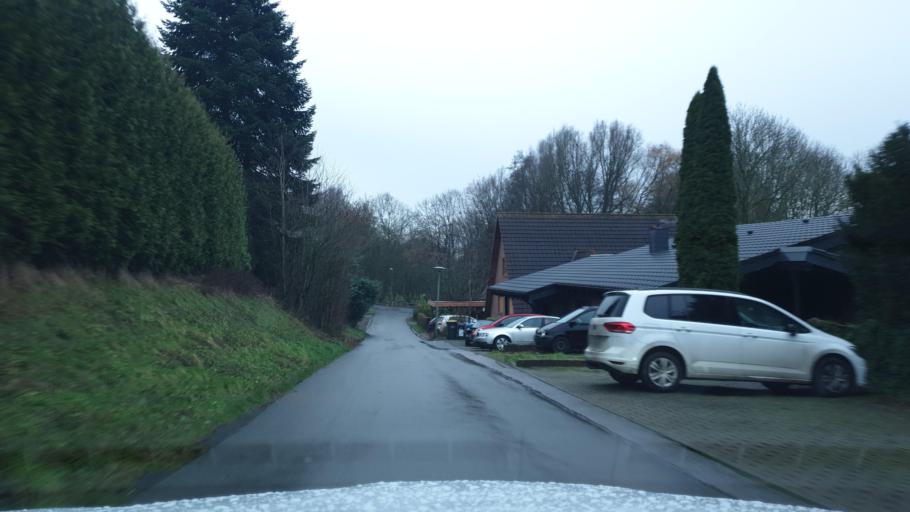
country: DE
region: North Rhine-Westphalia
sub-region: Regierungsbezirk Detmold
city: Hille
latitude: 52.2677
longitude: 8.7549
